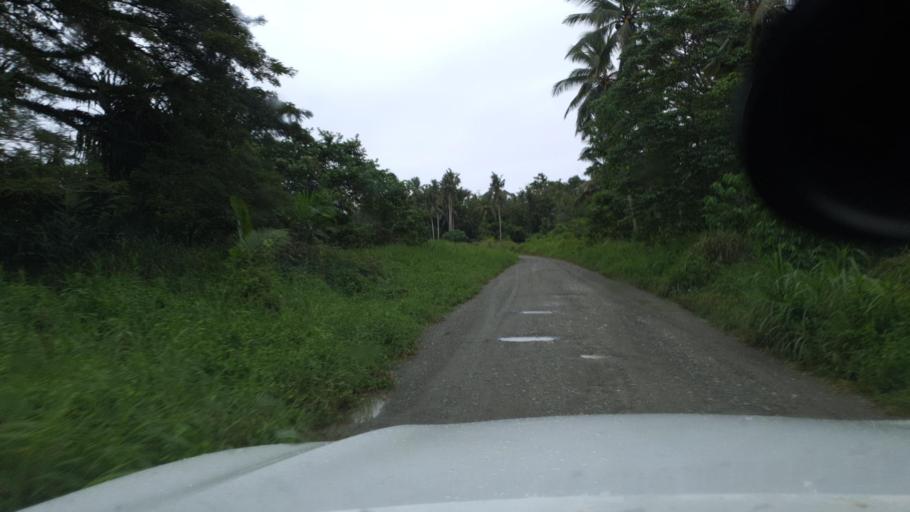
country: SB
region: Central Province
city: Tulaghi
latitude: -9.4523
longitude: 160.3913
